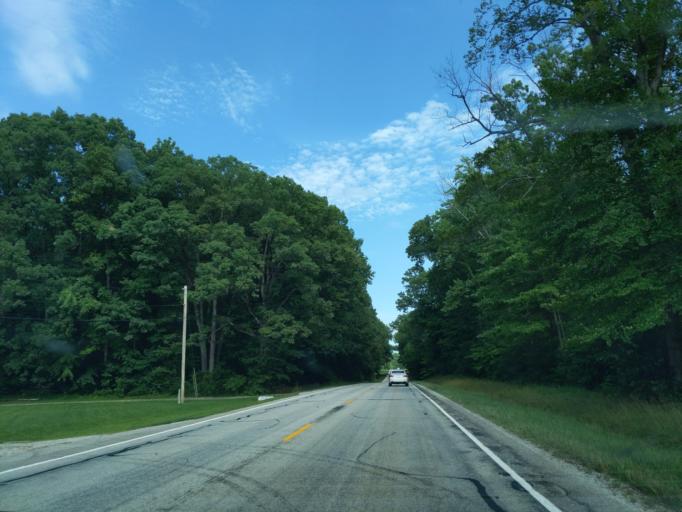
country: US
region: Indiana
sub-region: Ripley County
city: Sunman
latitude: 39.2778
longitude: -85.1261
